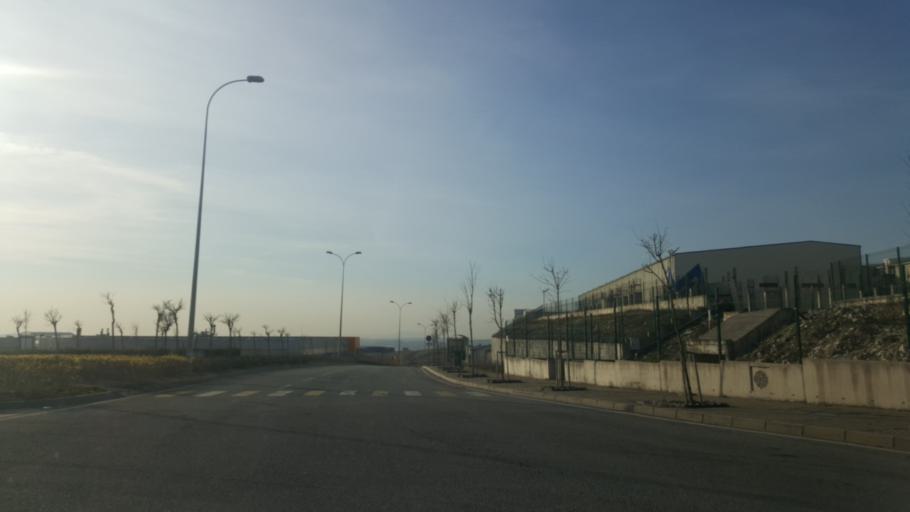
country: TR
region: Kocaeli
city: Tavsanli
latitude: 40.8310
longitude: 29.5581
